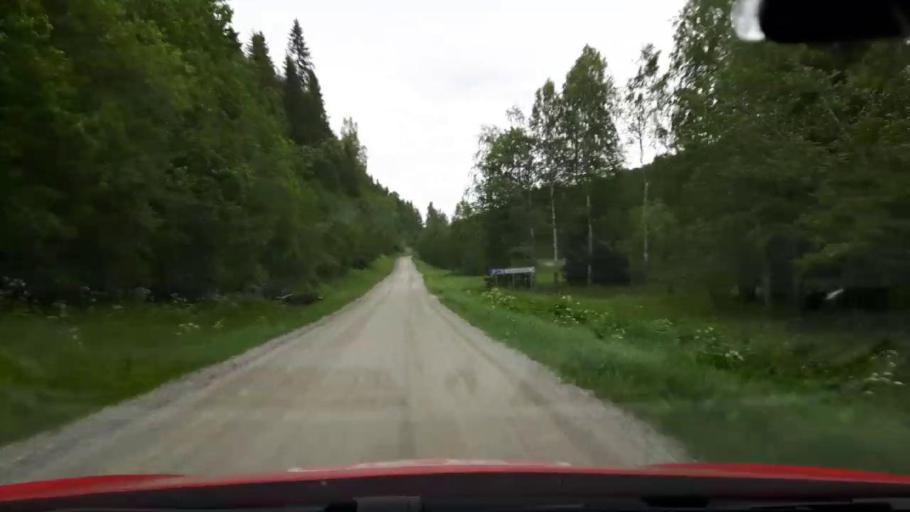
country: SE
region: Jaemtland
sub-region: Ragunda Kommun
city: Hammarstrand
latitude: 63.1939
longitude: 16.1346
